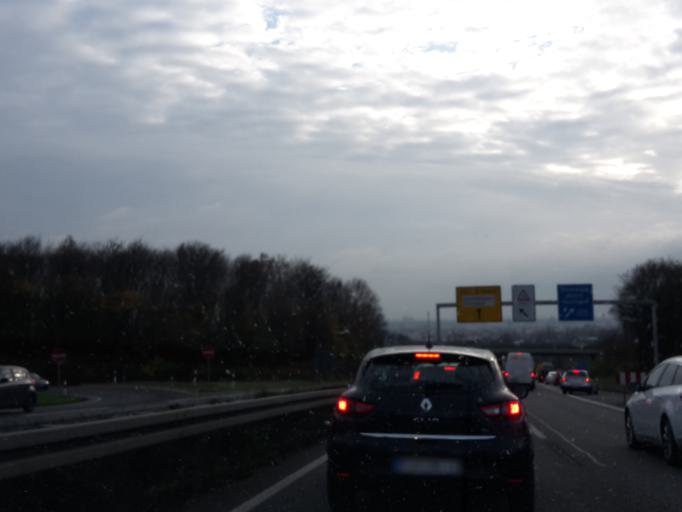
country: DE
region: Rheinland-Pfalz
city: Mainz
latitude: 50.0328
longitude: 8.2952
